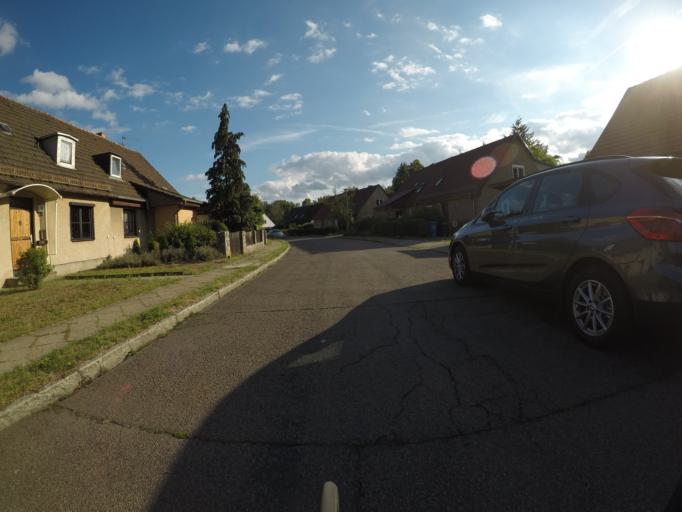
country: DE
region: Berlin
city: Stadtrandsiedlung Malchow
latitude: 52.5720
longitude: 13.4909
